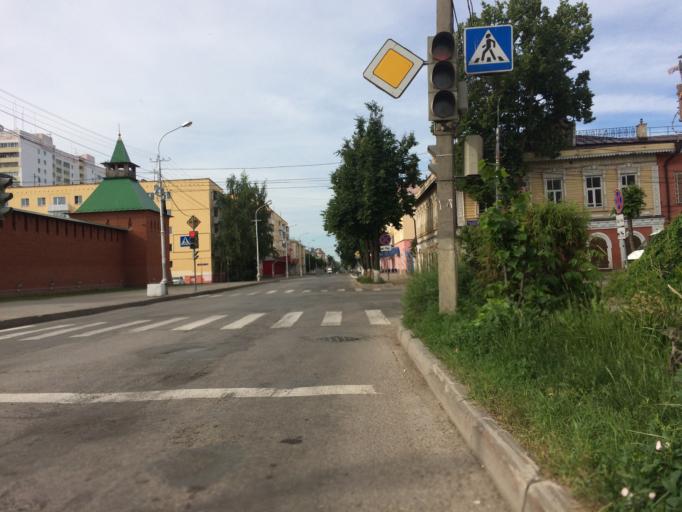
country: RU
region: Mariy-El
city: Yoshkar-Ola
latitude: 56.6378
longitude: 47.8995
